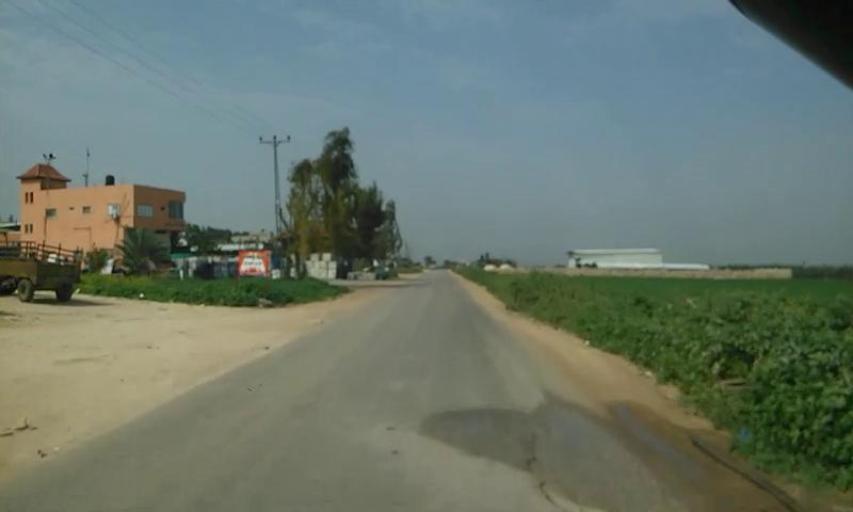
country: PS
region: West Bank
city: Kafr Dan
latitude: 32.4933
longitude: 35.2568
